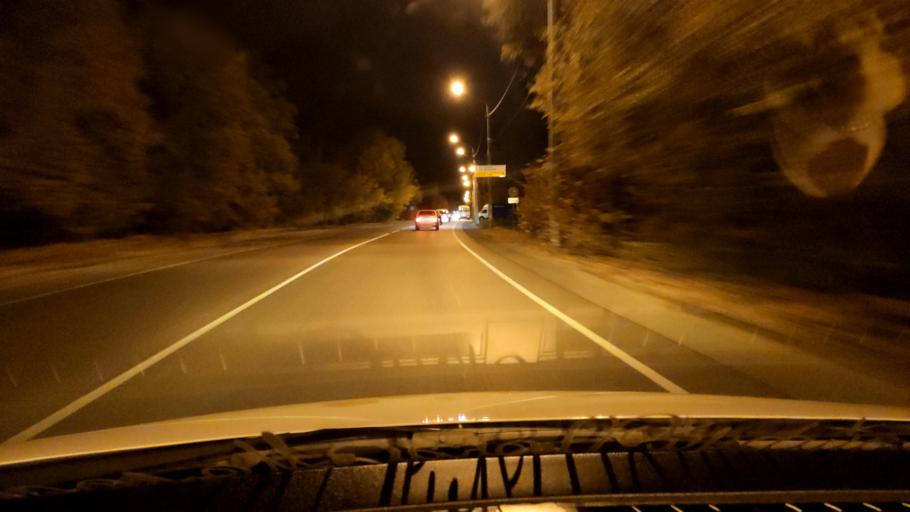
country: RU
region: Voronezj
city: Maslovka
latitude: 51.5952
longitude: 39.1768
